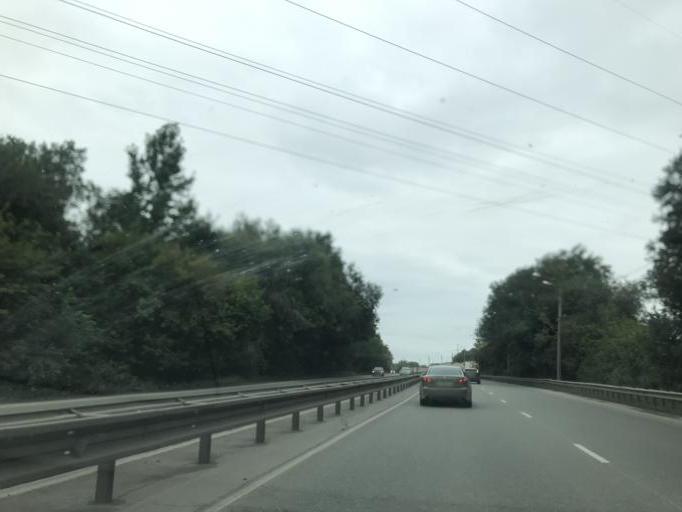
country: RU
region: Chelyabinsk
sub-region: Gorod Chelyabinsk
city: Chelyabinsk
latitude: 55.1712
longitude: 61.4272
